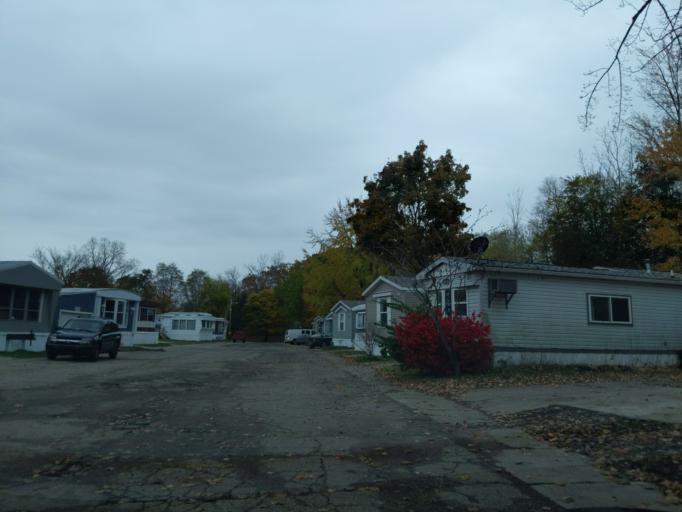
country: US
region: Michigan
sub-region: Ingham County
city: Edgemont Park
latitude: 42.7099
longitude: -84.5966
